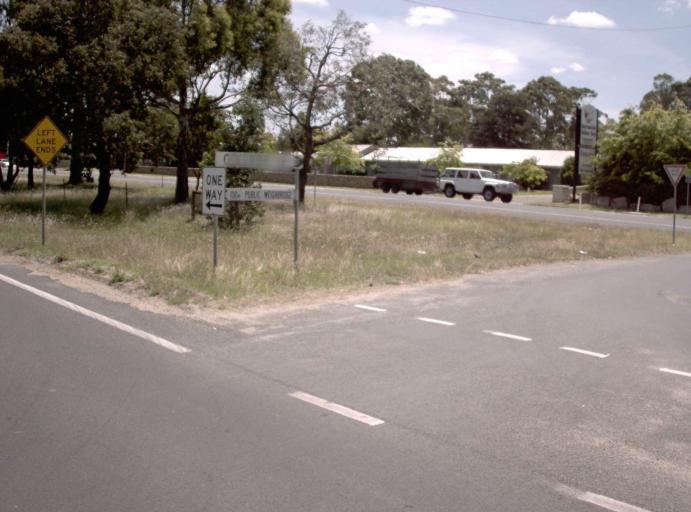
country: AU
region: Victoria
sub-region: East Gippsland
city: Bairnsdale
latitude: -37.8370
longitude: 147.5993
